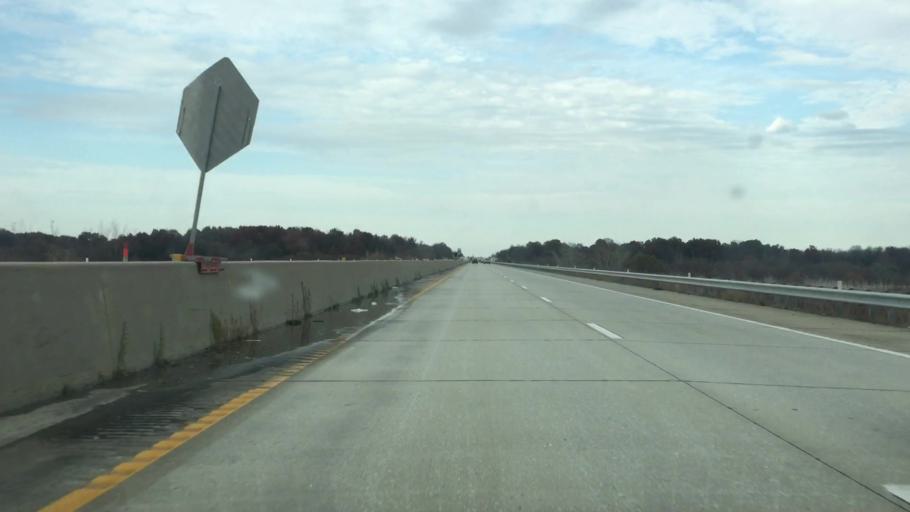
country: US
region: Missouri
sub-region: Henry County
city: Clinton
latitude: 38.2868
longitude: -93.7593
